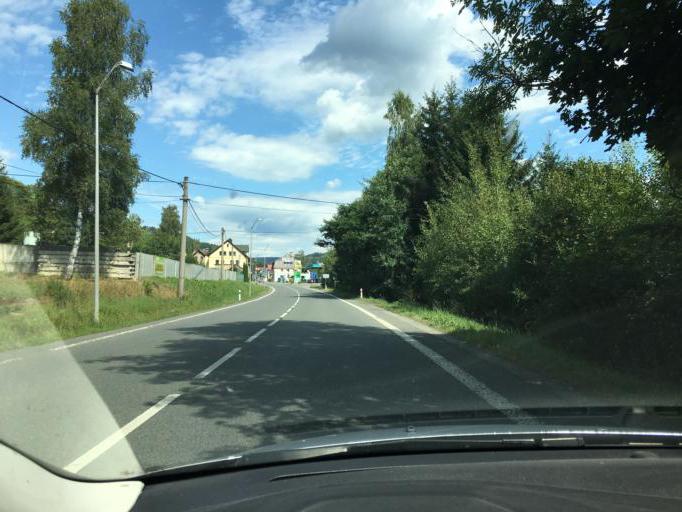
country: CZ
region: Liberecky
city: Velke Hamry
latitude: 50.7108
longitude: 15.3164
